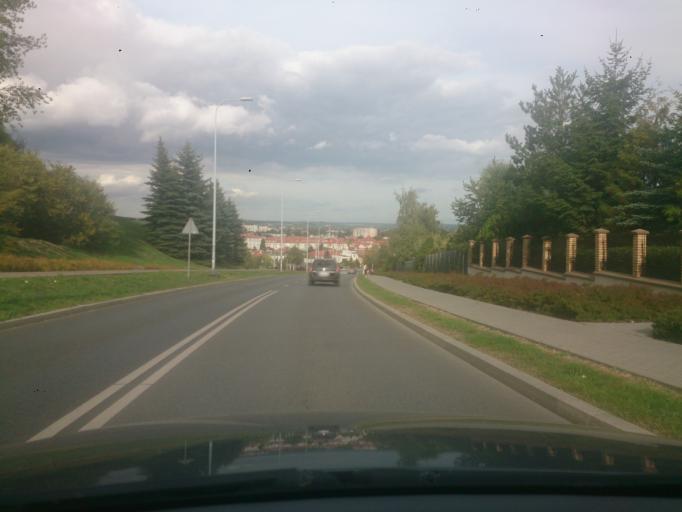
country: PL
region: Kujawsko-Pomorskie
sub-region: Grudziadz
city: Grudziadz
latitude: 53.4667
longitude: 18.7342
